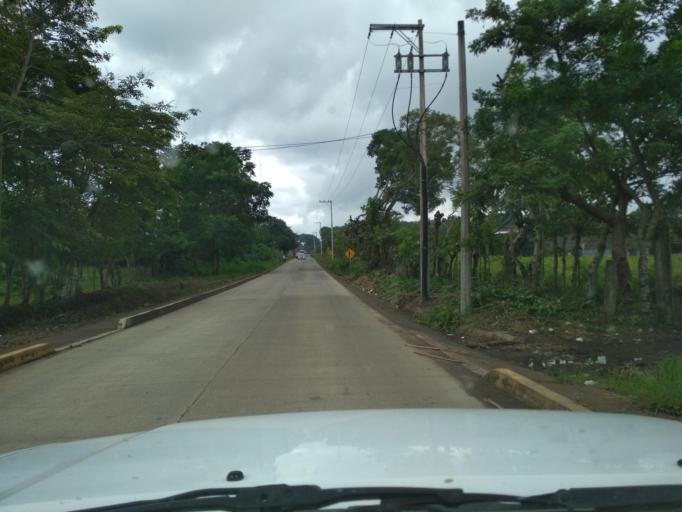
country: MX
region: Veracruz
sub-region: San Andres Tuxtla
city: Matacapan
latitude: 18.4245
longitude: -95.1772
